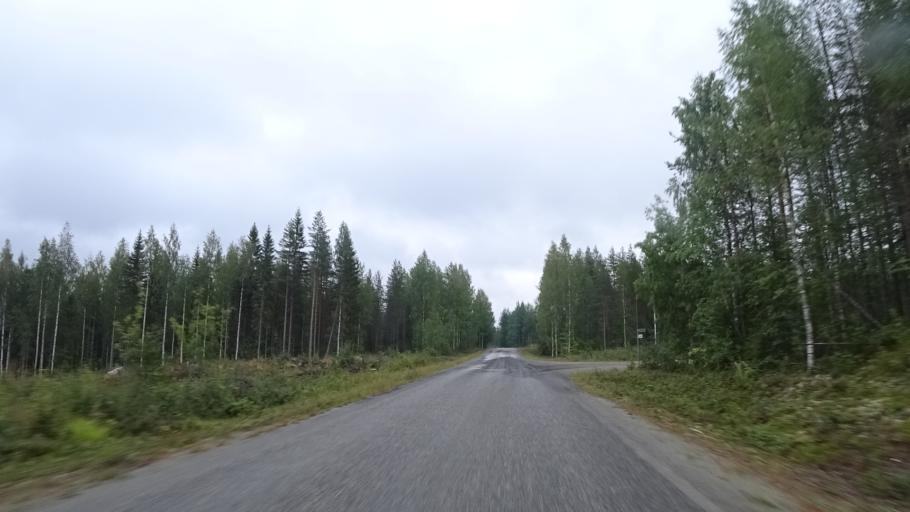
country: FI
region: North Karelia
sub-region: Joensuu
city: Ilomantsi
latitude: 63.2278
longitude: 30.8279
